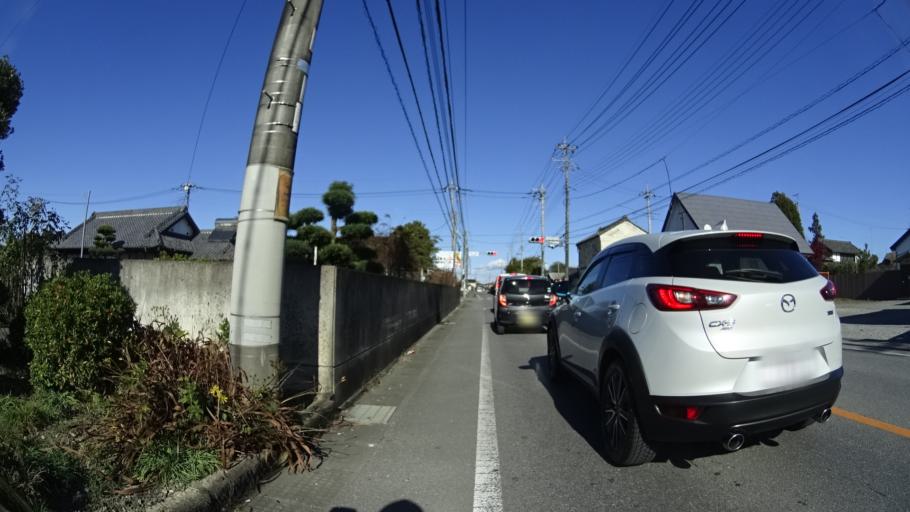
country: JP
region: Tochigi
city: Tochigi
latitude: 36.4150
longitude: 139.7482
